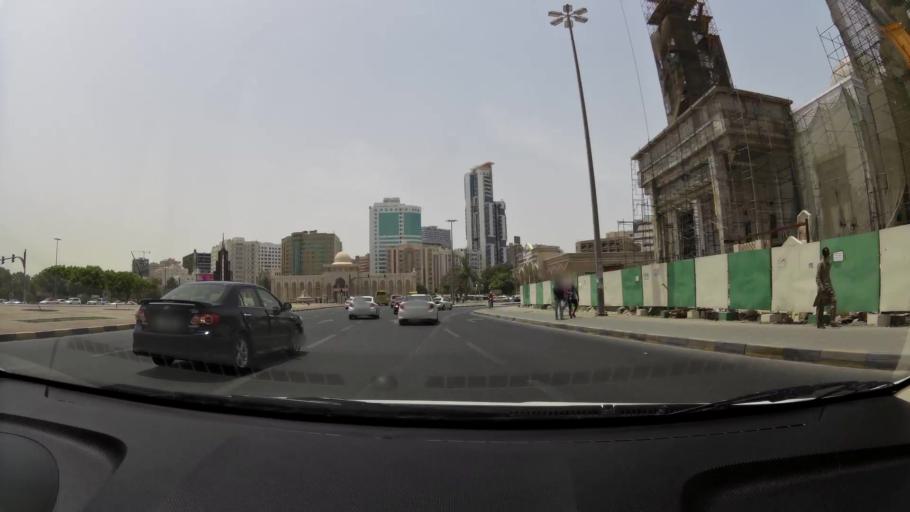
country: AE
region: Ash Shariqah
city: Sharjah
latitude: 25.3533
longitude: 55.3905
